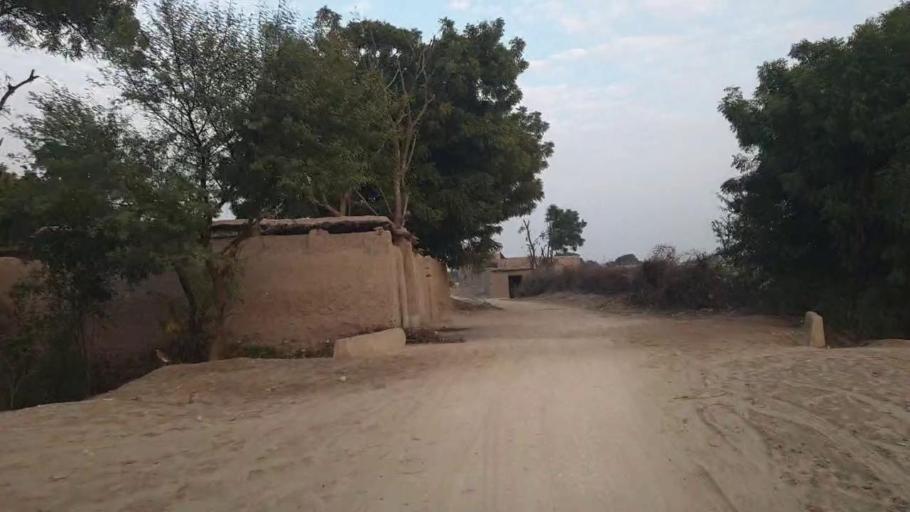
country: PK
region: Sindh
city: Shahpur Chakar
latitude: 26.0876
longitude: 68.5502
